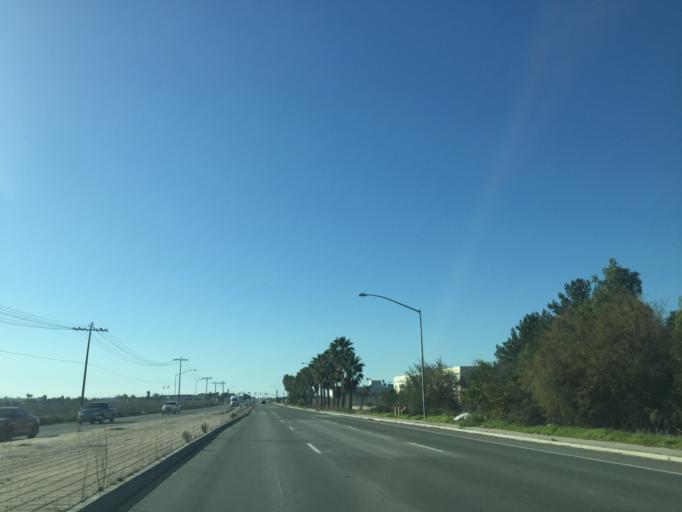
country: MX
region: Baja California
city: Tijuana
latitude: 32.5678
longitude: -116.9572
